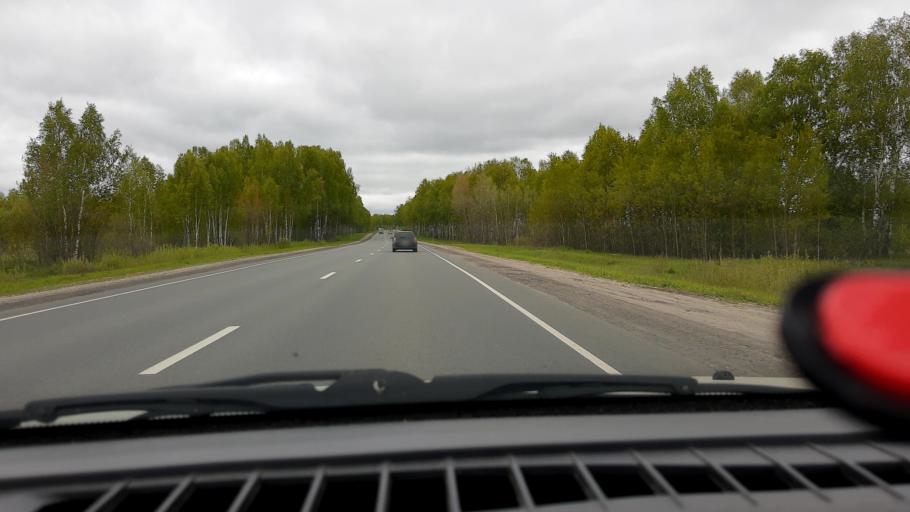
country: RU
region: Nizjnij Novgorod
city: Linda
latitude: 56.5893
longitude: 44.0348
